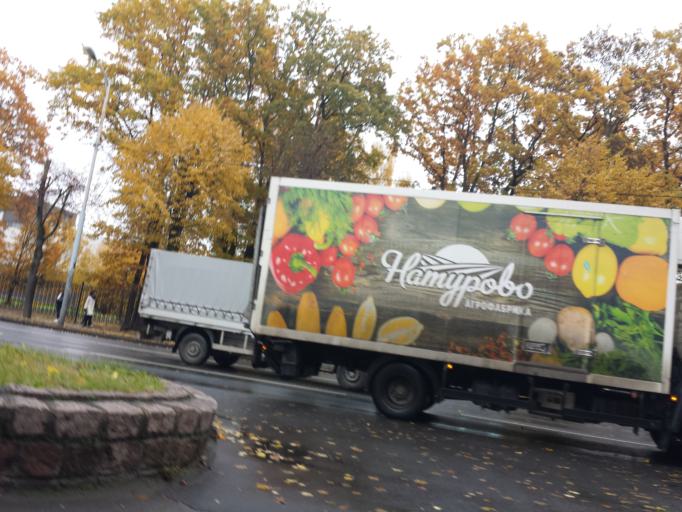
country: RU
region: Kaliningrad
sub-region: Gorod Kaliningrad
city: Kaliningrad
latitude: 54.7247
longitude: 20.5260
